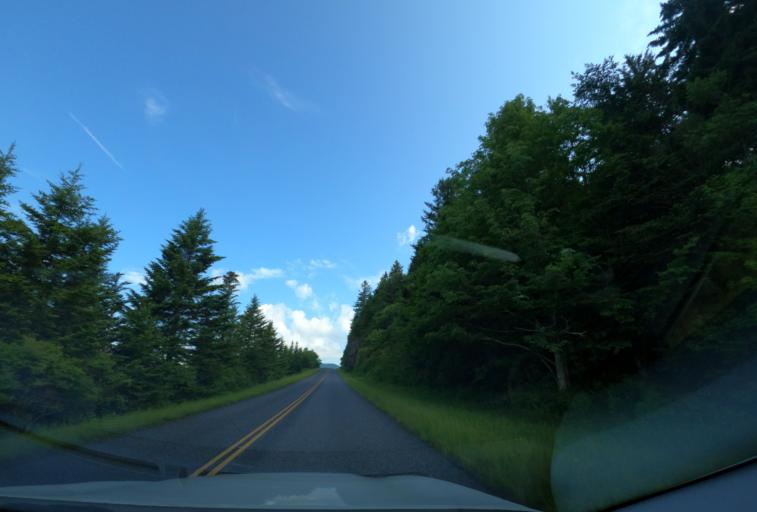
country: US
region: North Carolina
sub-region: Haywood County
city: Hazelwood
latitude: 35.3254
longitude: -82.9644
